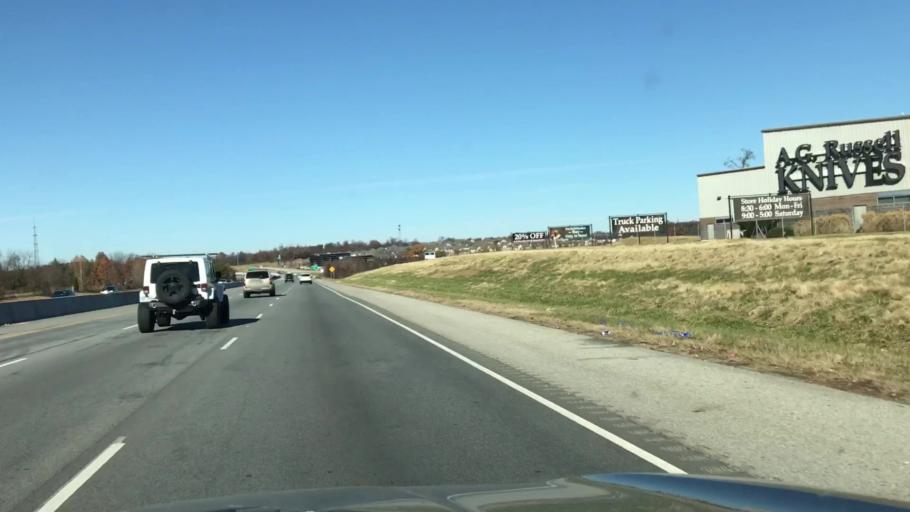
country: US
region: Arkansas
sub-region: Benton County
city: Lowell
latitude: 36.2888
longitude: -94.1608
